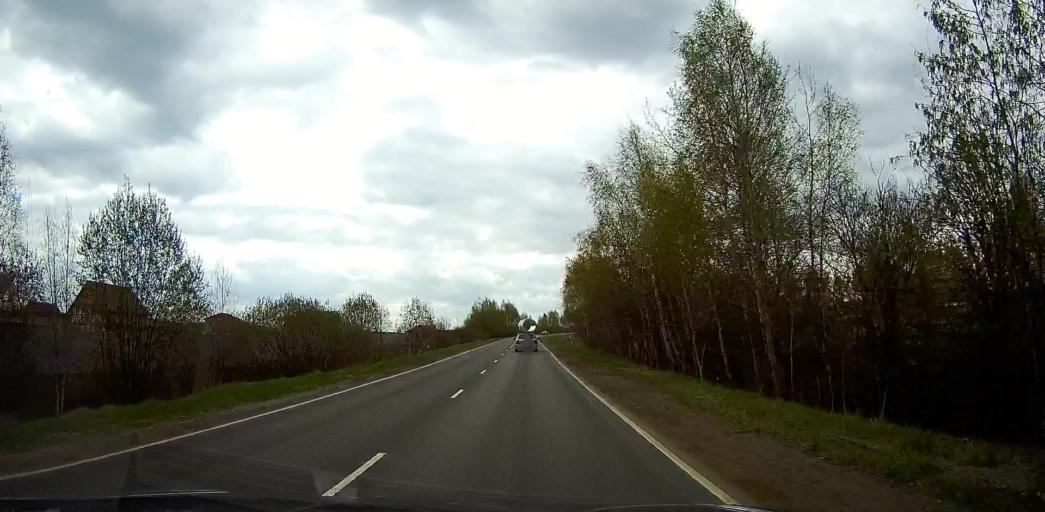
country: RU
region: Moskovskaya
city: Beloozerskiy
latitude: 55.5238
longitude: 38.4338
